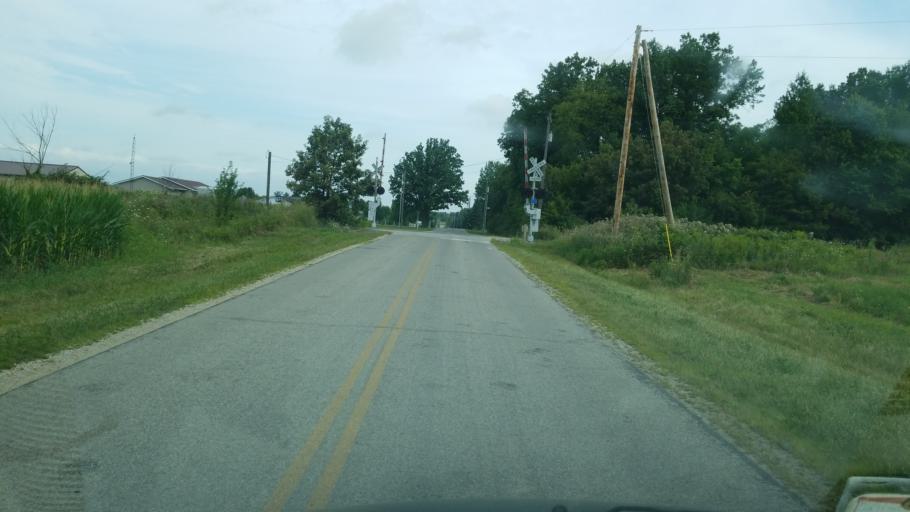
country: US
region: Ohio
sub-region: Seneca County
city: Tiffin
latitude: 41.1177
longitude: -83.0941
